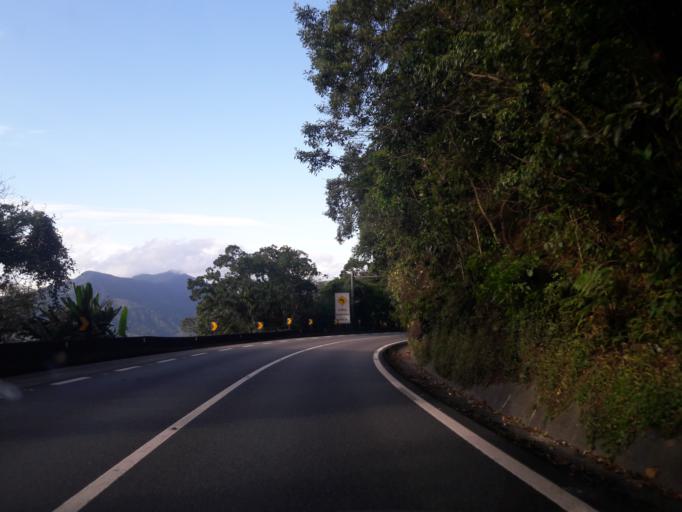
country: BR
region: Sao Paulo
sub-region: Cubatao
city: Cubatao
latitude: -23.8890
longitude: -46.4894
